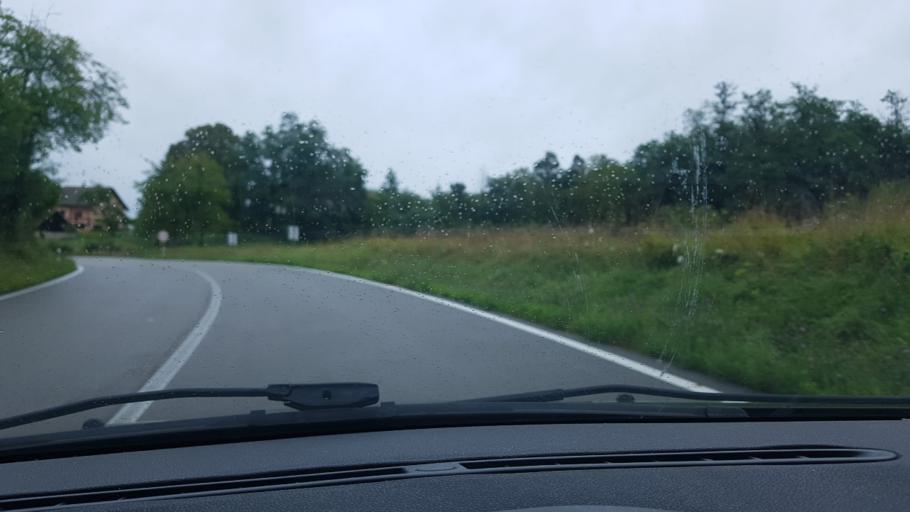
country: HR
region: Primorsko-Goranska
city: Vrbovsko
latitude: 45.4219
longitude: 15.2184
